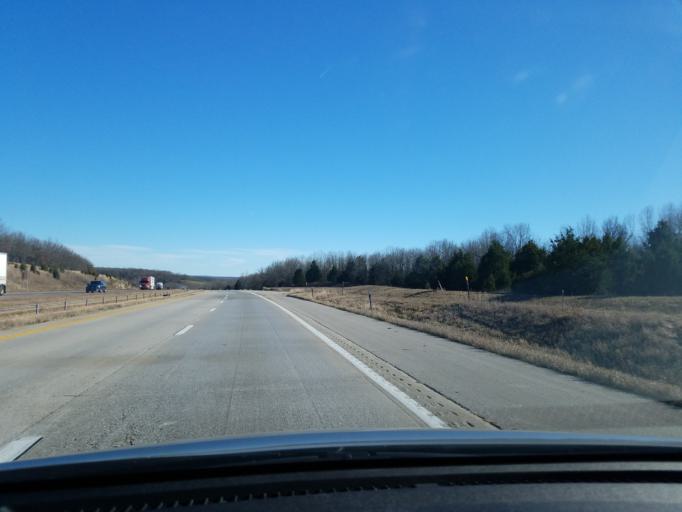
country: US
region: Missouri
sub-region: Pulaski County
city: Richland
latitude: 37.7546
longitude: -92.5030
